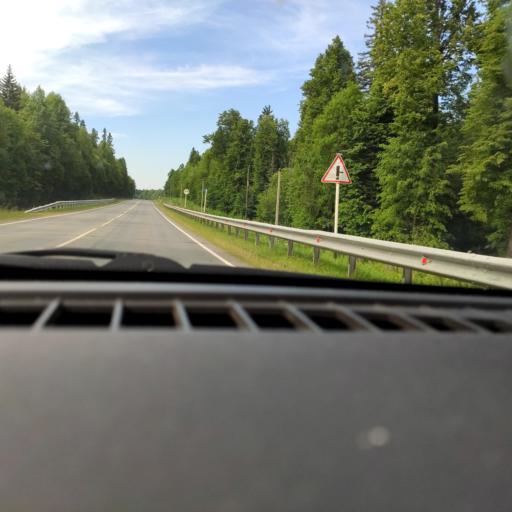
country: RU
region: Perm
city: Polazna
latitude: 58.3062
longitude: 56.1549
